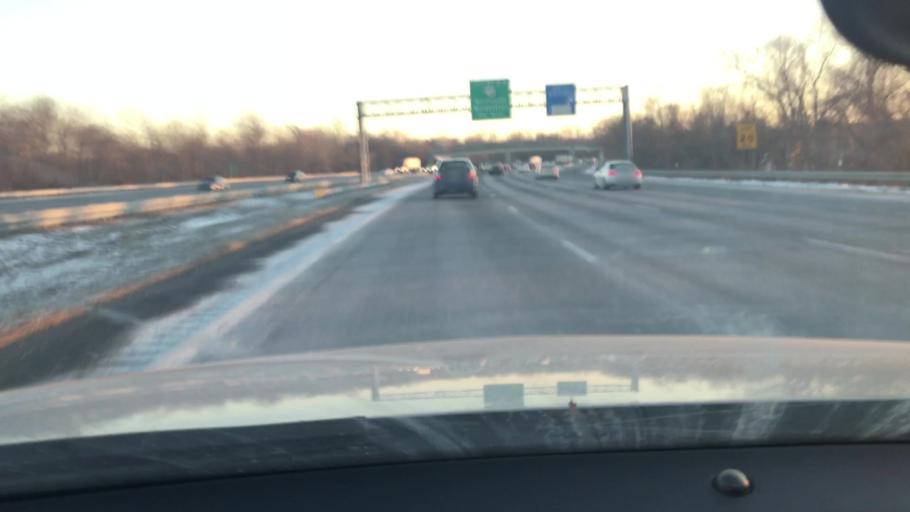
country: US
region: New Jersey
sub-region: Burlington County
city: Bordentown
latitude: 40.1590
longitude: -74.7184
